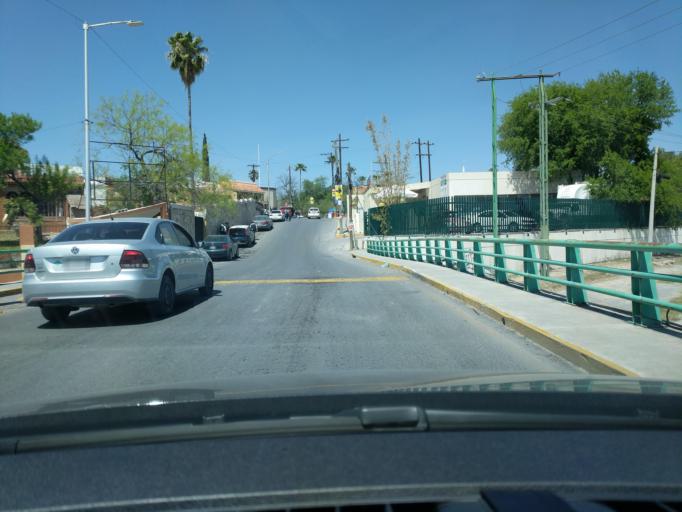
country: MX
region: Nuevo Leon
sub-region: Salinas Victoria
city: Las Torres
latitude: 25.9587
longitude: -100.2911
